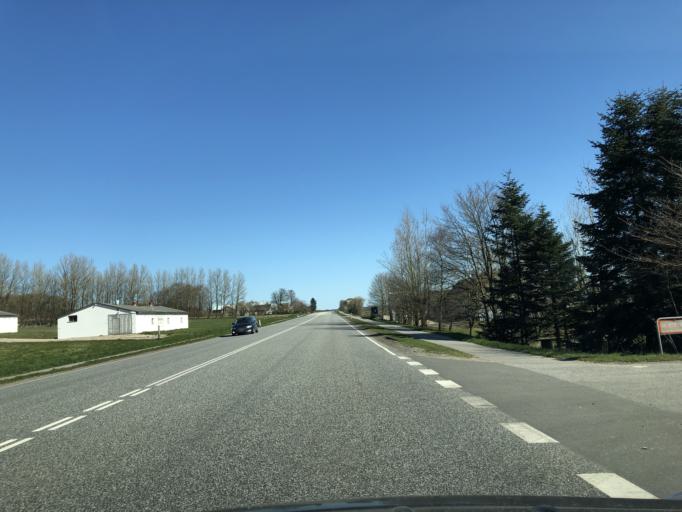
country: DK
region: North Denmark
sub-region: Rebild Kommune
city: Stovring
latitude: 56.9128
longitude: 9.8517
